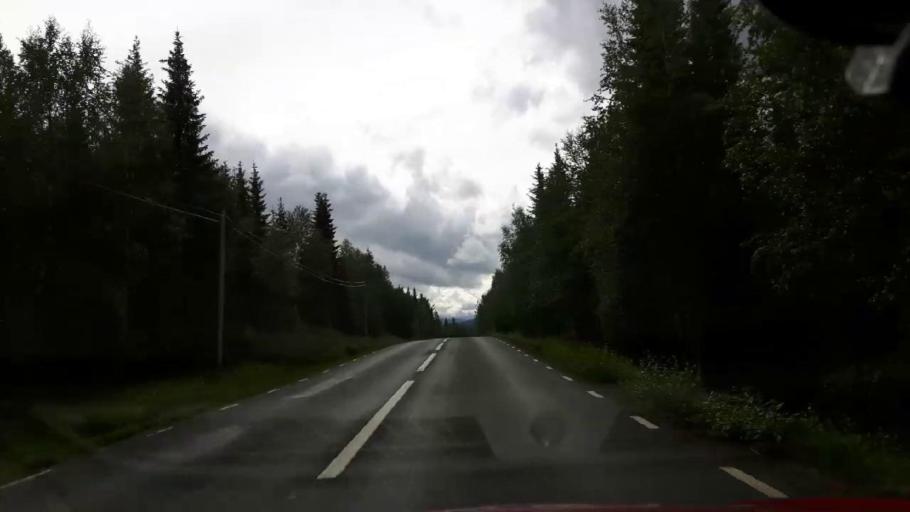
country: NO
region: Nord-Trondelag
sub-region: Lierne
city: Sandvika
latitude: 64.5214
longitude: 14.1635
